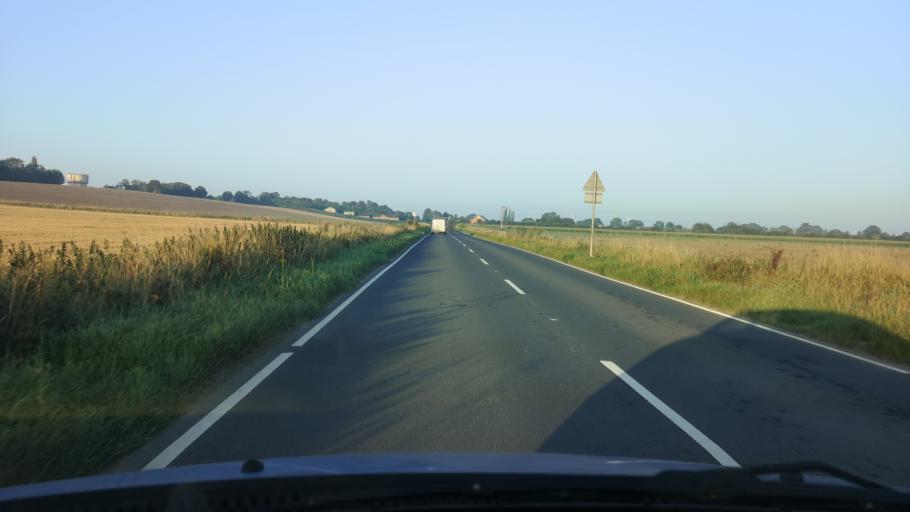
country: GB
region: England
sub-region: North Lincolnshire
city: Crowle
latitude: 53.6144
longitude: -0.8205
